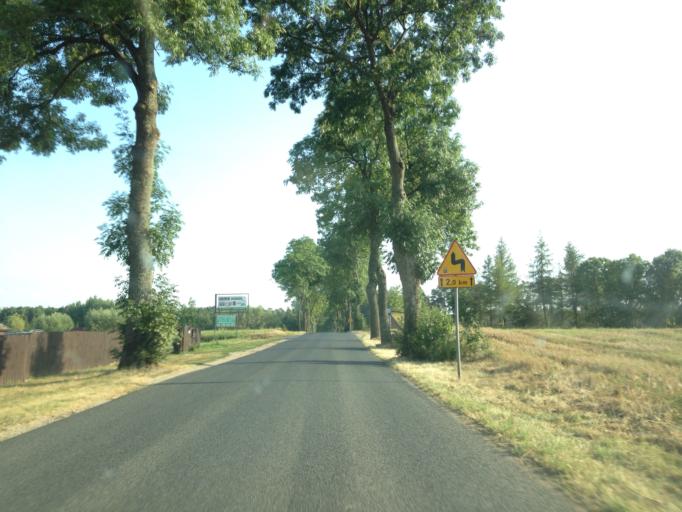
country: PL
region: Kujawsko-Pomorskie
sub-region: Powiat brodnicki
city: Brodnica
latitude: 53.3680
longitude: 19.3757
